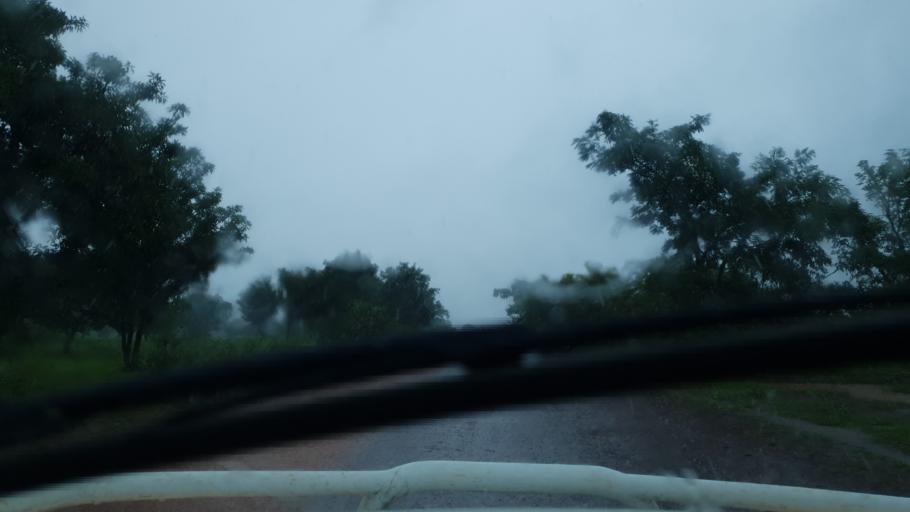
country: ML
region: Sikasso
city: Kolondieba
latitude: 11.6169
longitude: -6.6778
